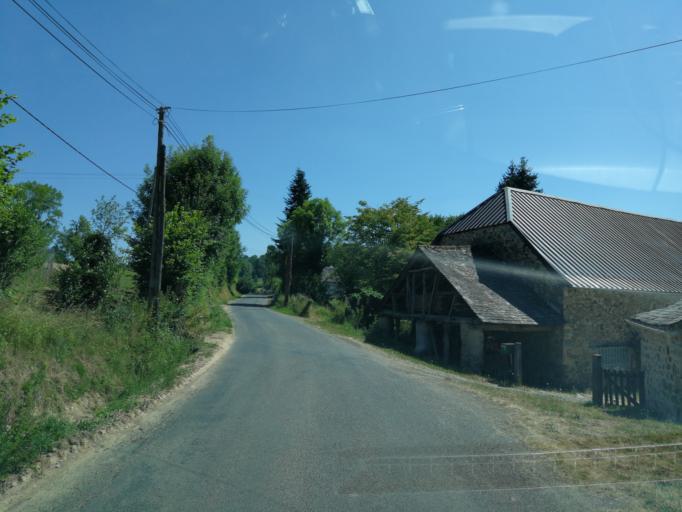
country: FR
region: Limousin
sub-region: Departement de la Correze
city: Sainte-Fereole
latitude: 45.2400
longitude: 1.5936
